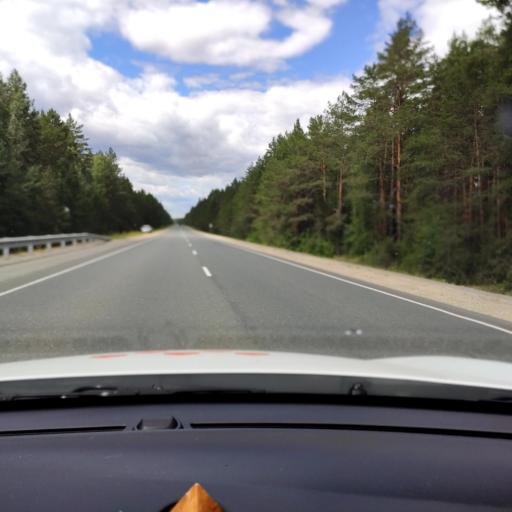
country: RU
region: Mariy-El
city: Pomary
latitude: 56.0438
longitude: 48.3772
